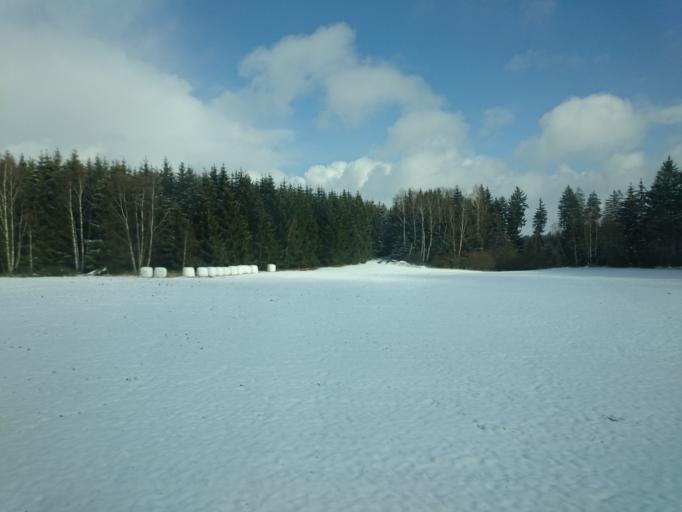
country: DE
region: Thuringia
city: Mossbach
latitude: 50.6754
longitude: 11.7863
